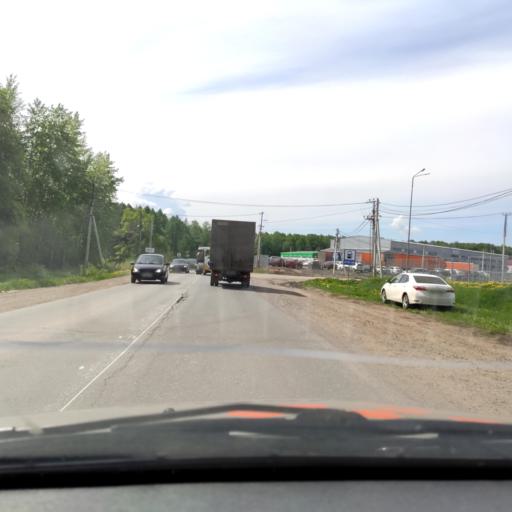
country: RU
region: Bashkortostan
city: Avdon
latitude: 54.6573
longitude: 55.7014
